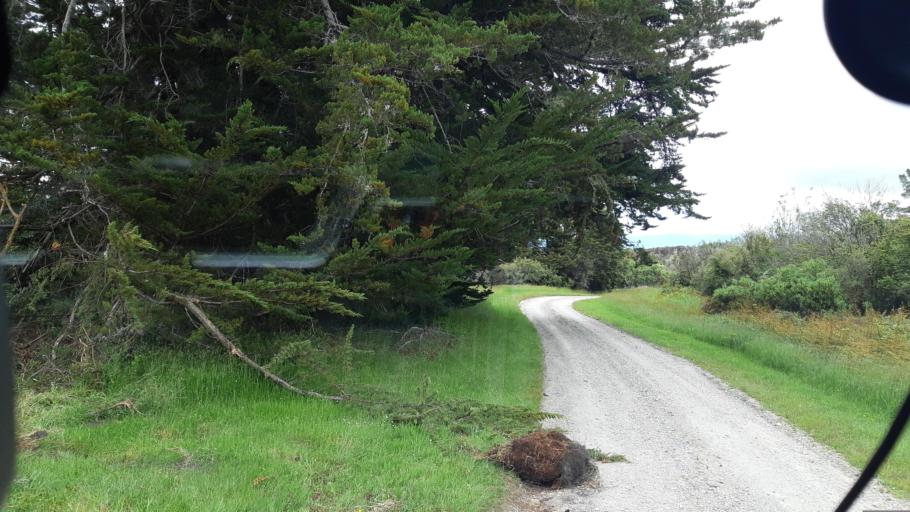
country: NZ
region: West Coast
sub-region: Buller District
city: Westport
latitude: -42.2957
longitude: 171.8241
